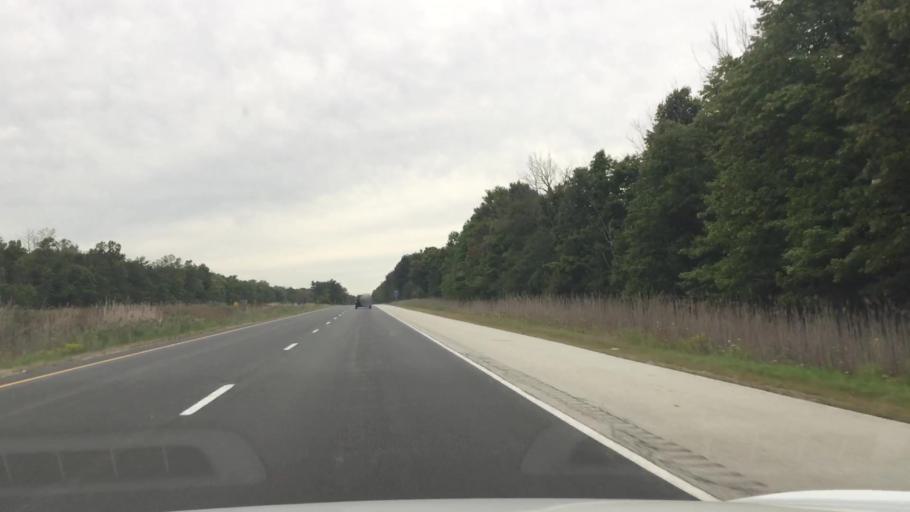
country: CA
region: Ontario
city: Camlachie
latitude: 42.9915
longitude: -82.0164
